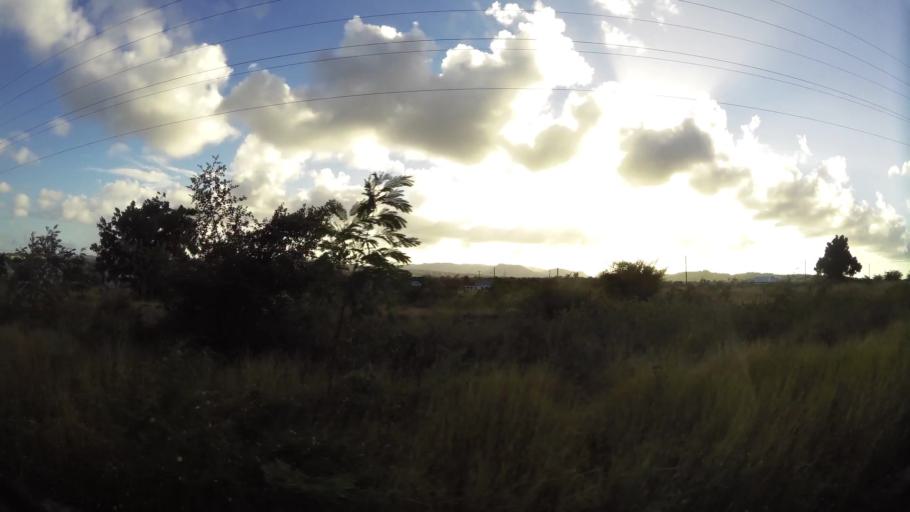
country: AG
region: Saint George
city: Piggotts
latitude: 17.1149
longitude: -61.7927
